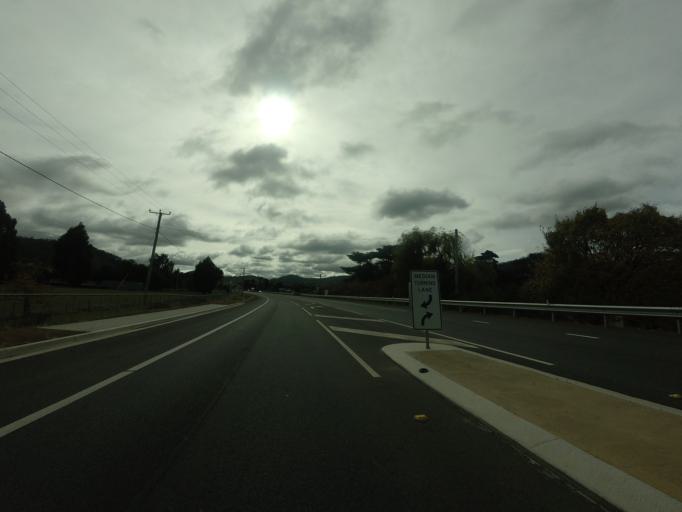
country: AU
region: Tasmania
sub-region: Brighton
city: Bridgewater
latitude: -42.6133
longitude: 147.2229
